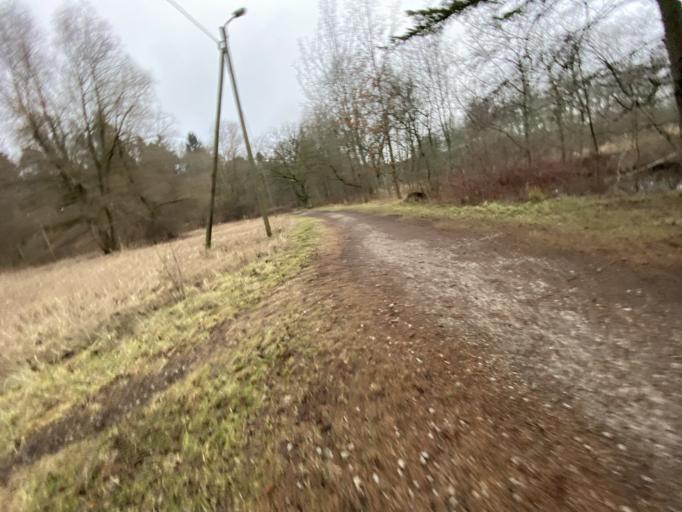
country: EE
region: Harju
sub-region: Tallinna linn
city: Kose
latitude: 59.4621
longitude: 24.8442
